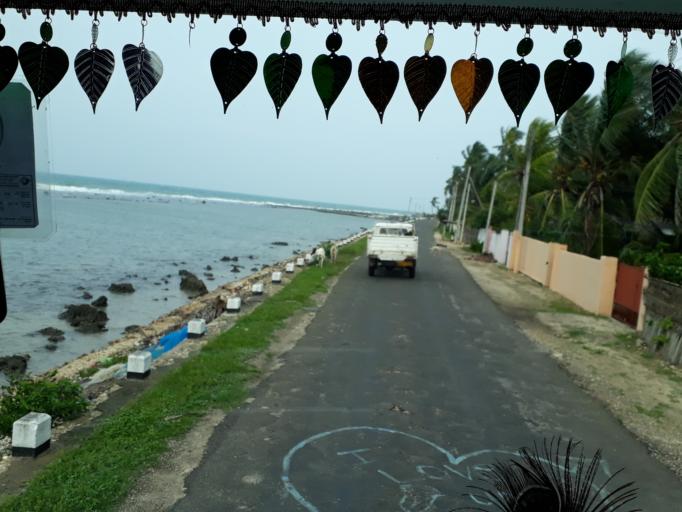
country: LK
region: Northern Province
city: Point Pedro
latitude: 9.8338
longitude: 80.2057
